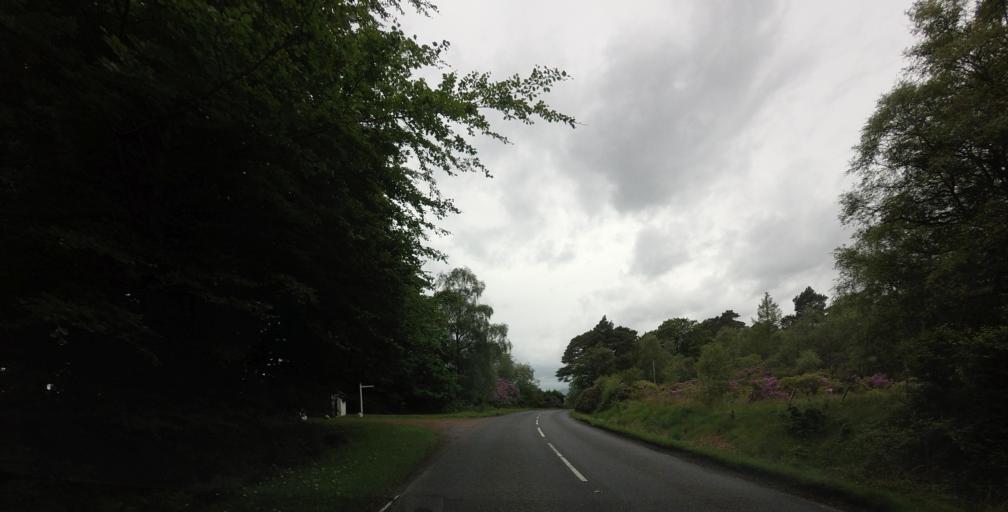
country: GB
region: Scotland
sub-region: Highland
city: Fort William
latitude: 56.7117
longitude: -5.2759
